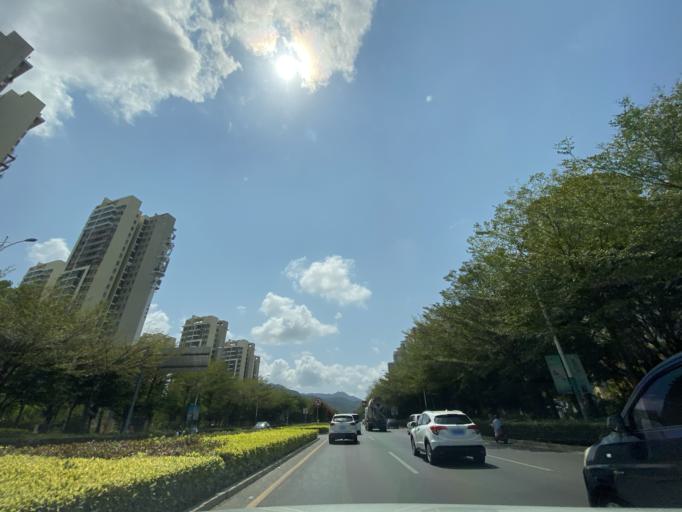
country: CN
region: Hainan
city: Tiandu
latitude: 18.2982
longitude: 109.5277
